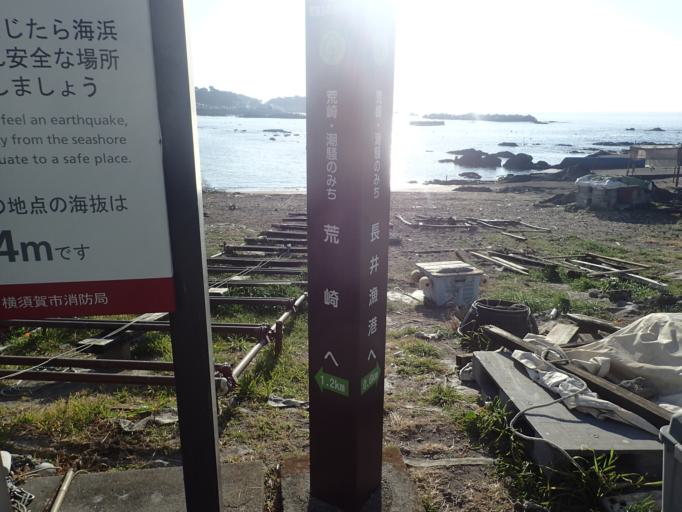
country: JP
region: Kanagawa
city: Miura
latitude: 35.2021
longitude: 139.6053
